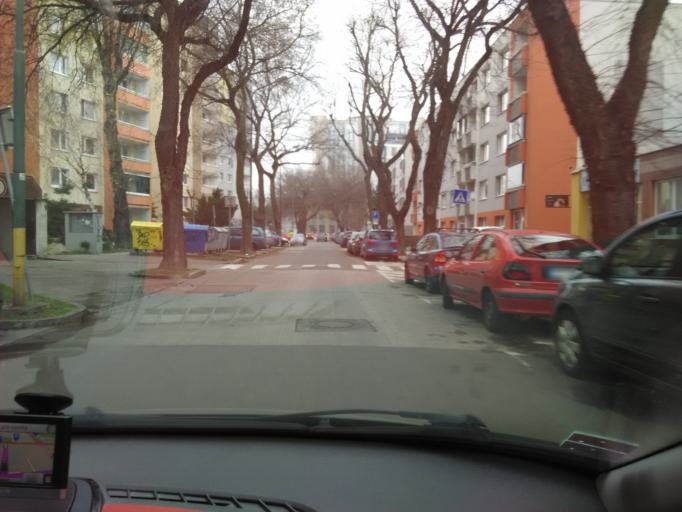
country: SK
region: Bratislavsky
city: Bratislava
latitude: 48.1587
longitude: 17.1395
